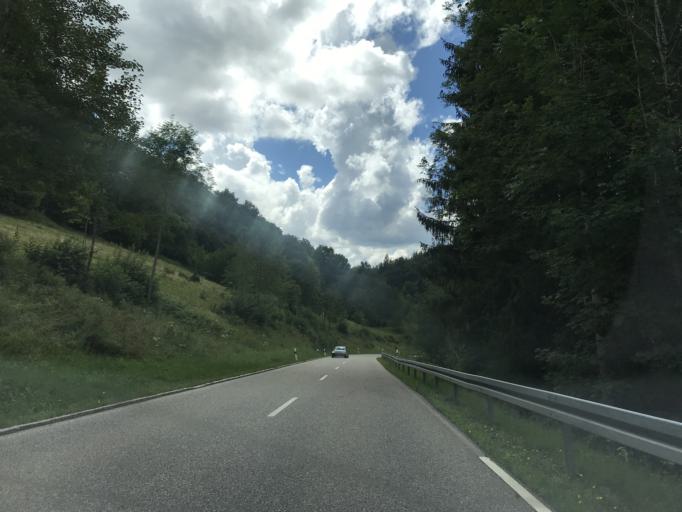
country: DE
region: Baden-Wuerttemberg
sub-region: Freiburg Region
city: Todtnau
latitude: 47.8394
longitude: 7.9376
